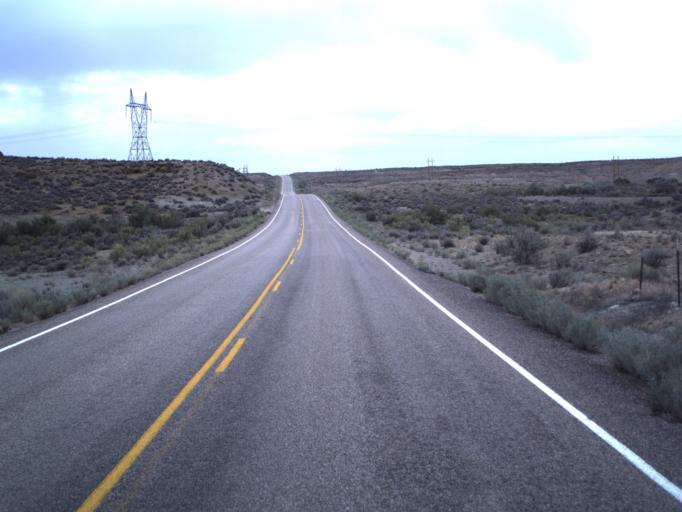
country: US
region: Colorado
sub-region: Rio Blanco County
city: Rangely
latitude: 40.0688
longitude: -109.2018
